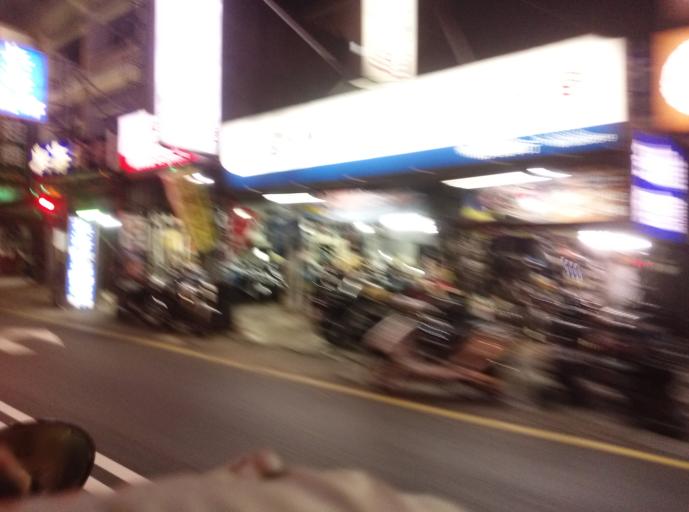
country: TW
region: Taiwan
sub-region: Hsinchu
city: Hsinchu
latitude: 24.8035
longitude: 120.9798
